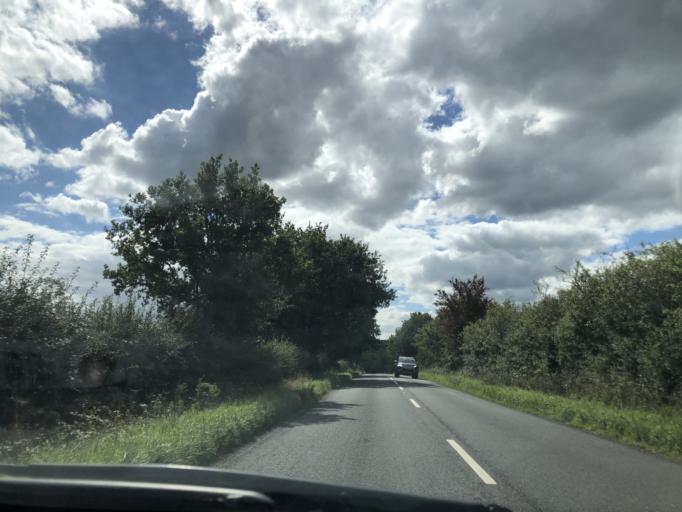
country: GB
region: England
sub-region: Kent
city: Halstead
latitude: 51.2843
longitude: 0.1291
